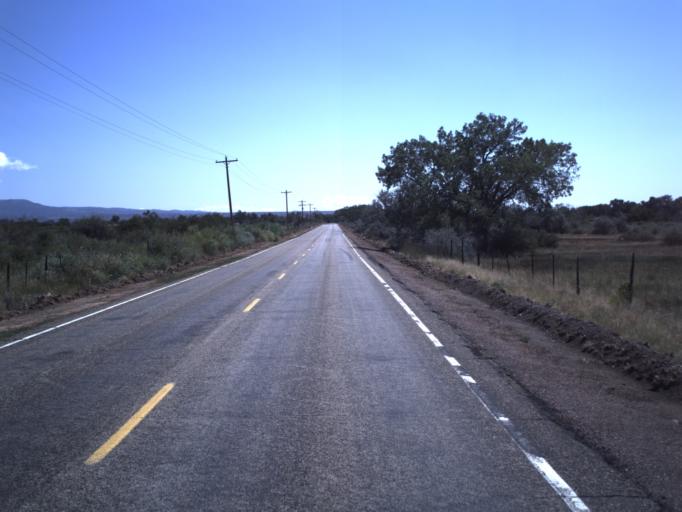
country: US
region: Utah
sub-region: Duchesne County
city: Roosevelt
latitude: 40.4329
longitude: -109.9425
